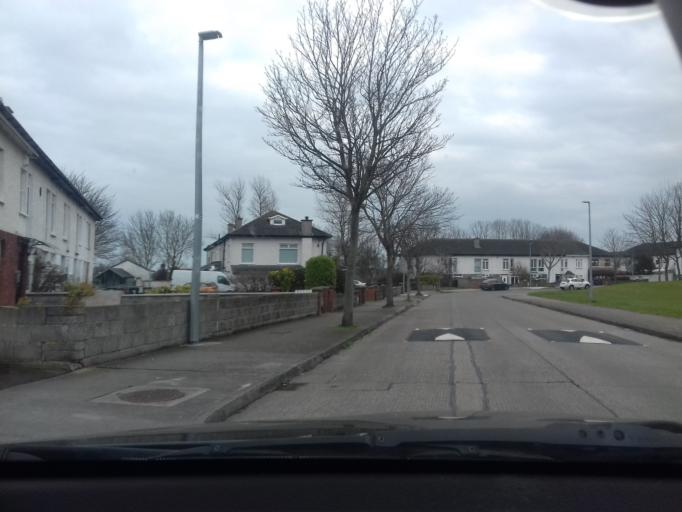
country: IE
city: Bayside
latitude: 53.3943
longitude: -6.1384
